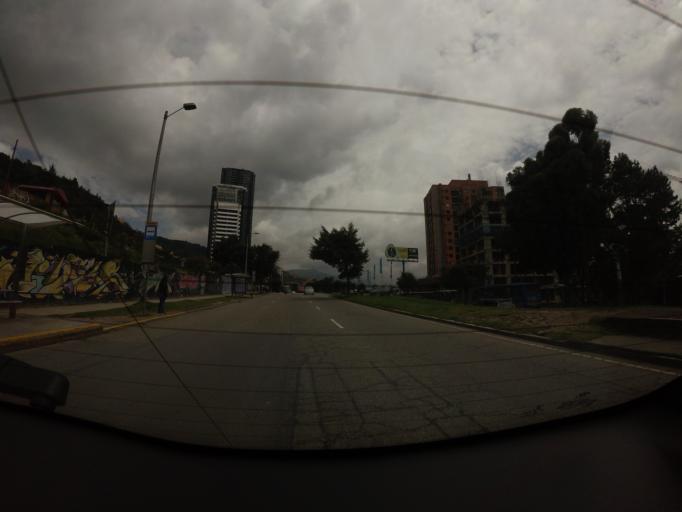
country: CO
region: Cundinamarca
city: La Calera
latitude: 4.7351
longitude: -74.0242
